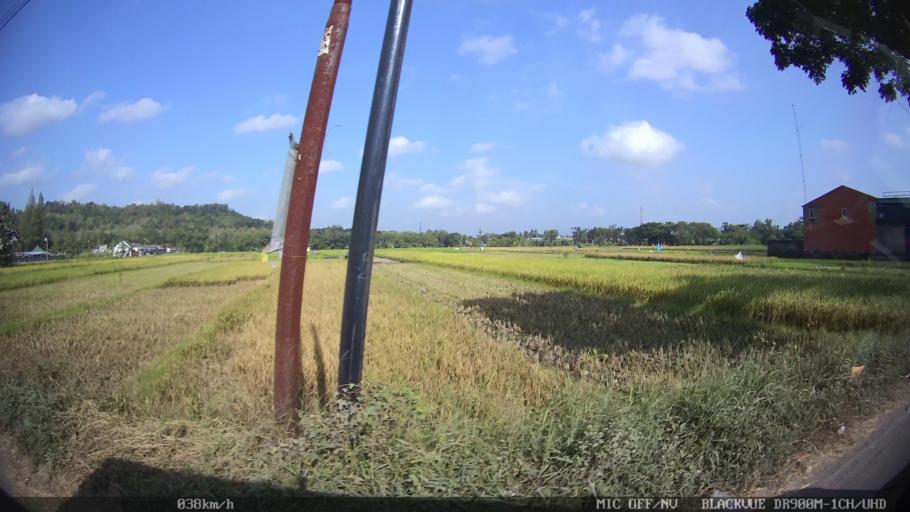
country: ID
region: Daerah Istimewa Yogyakarta
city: Gamping Lor
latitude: -7.8086
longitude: 110.2995
